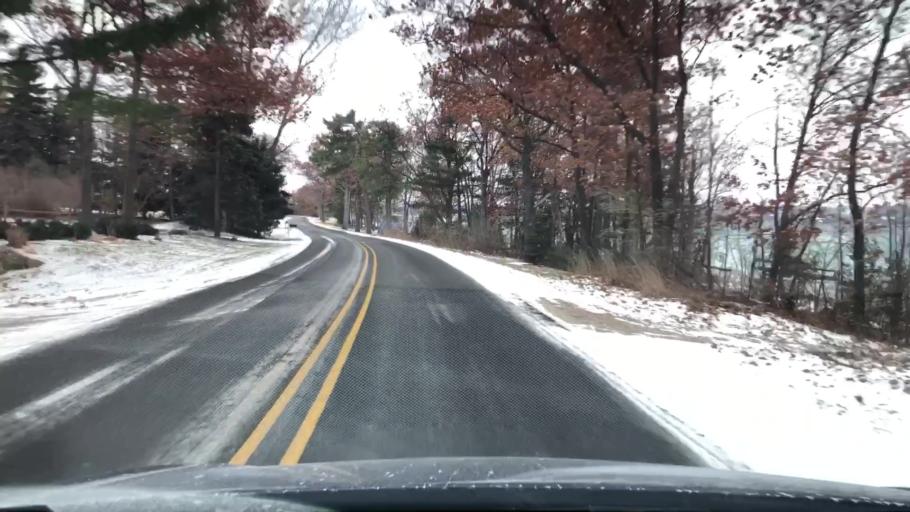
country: US
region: Michigan
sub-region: Grand Traverse County
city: Traverse City
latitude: 44.8118
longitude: -85.5794
